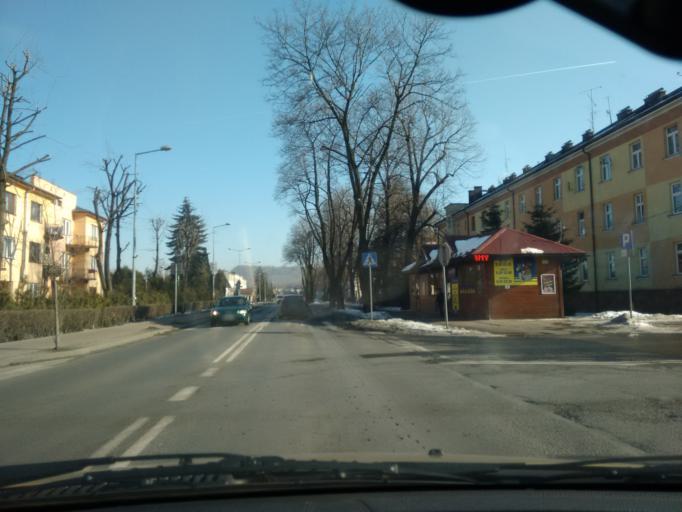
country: PL
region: Lesser Poland Voivodeship
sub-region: Powiat wadowicki
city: Andrychow
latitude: 49.8564
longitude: 19.3322
